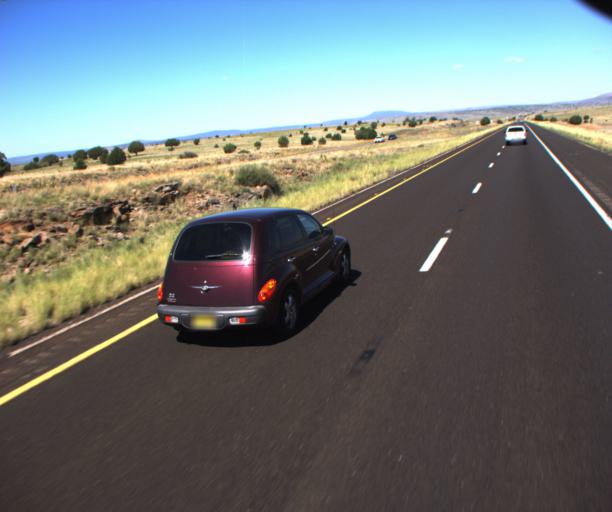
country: US
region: Arizona
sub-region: Yavapai County
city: Paulden
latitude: 35.2845
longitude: -112.7987
